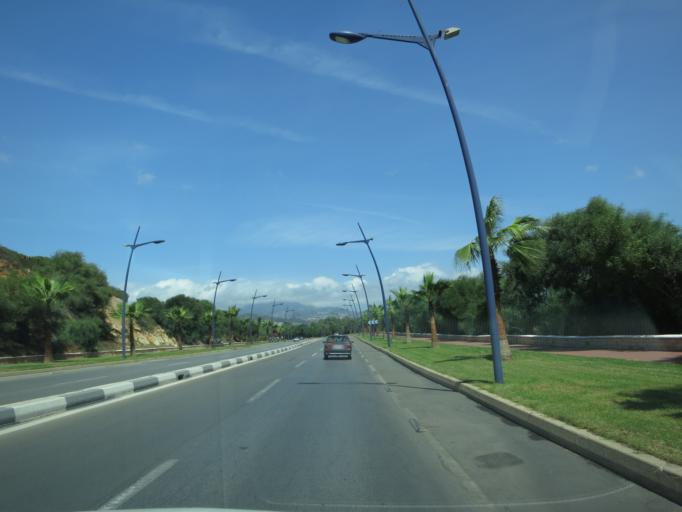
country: ES
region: Ceuta
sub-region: Ceuta
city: Ceuta
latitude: 35.7836
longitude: -5.3509
